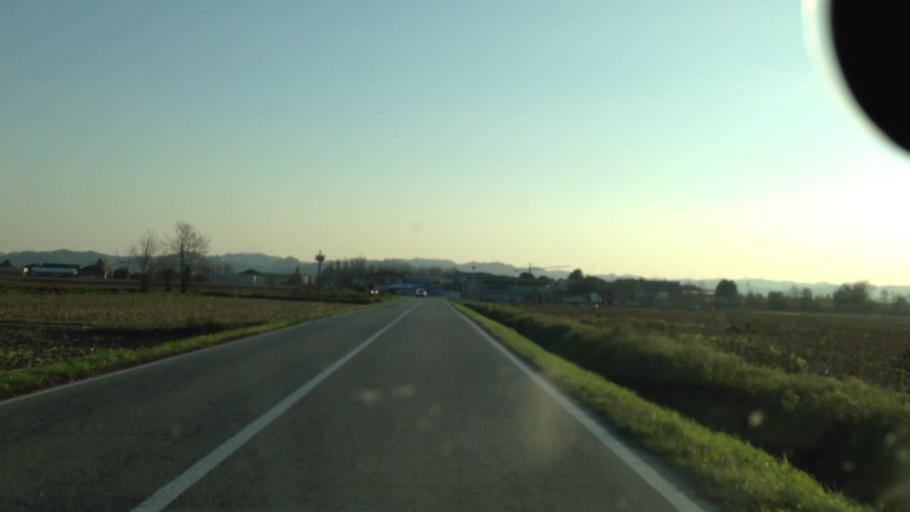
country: IT
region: Piedmont
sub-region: Provincia di Vercelli
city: Crescentino
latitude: 45.2047
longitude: 8.1037
